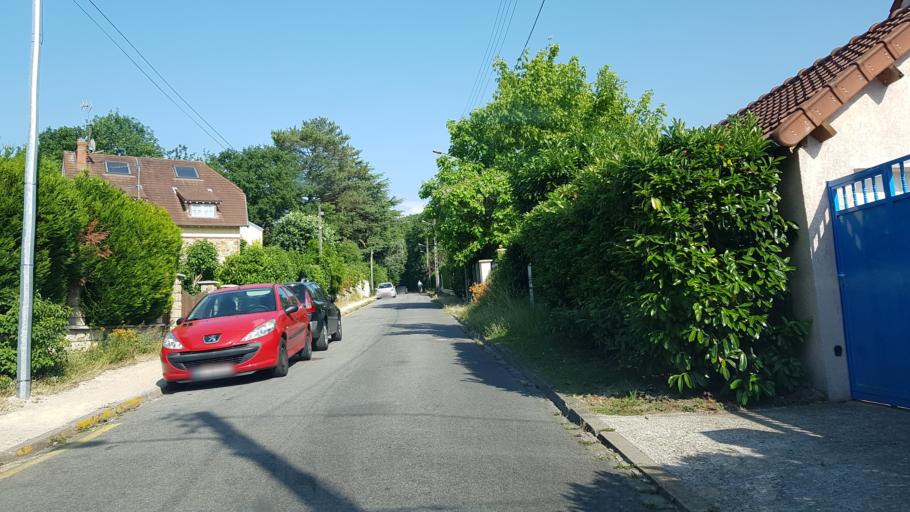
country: FR
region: Ile-de-France
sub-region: Departement des Yvelines
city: Saint-Remy-les-Chevreuse
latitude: 48.7009
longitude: 2.0729
